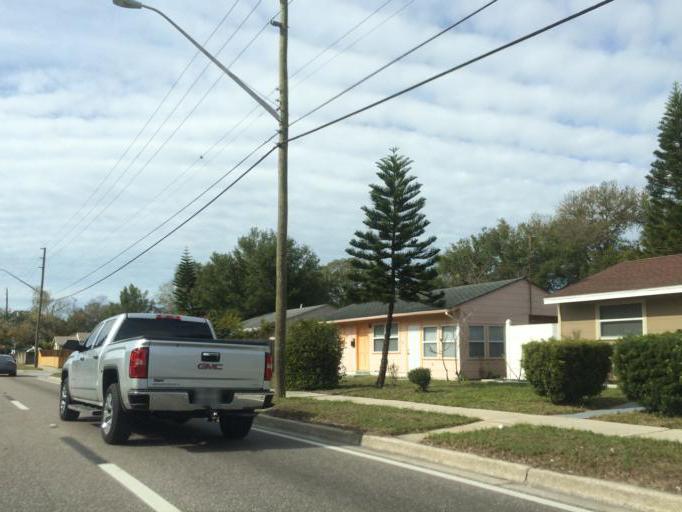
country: US
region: Florida
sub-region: Pinellas County
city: West and East Lealman
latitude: 27.8065
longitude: -82.6850
